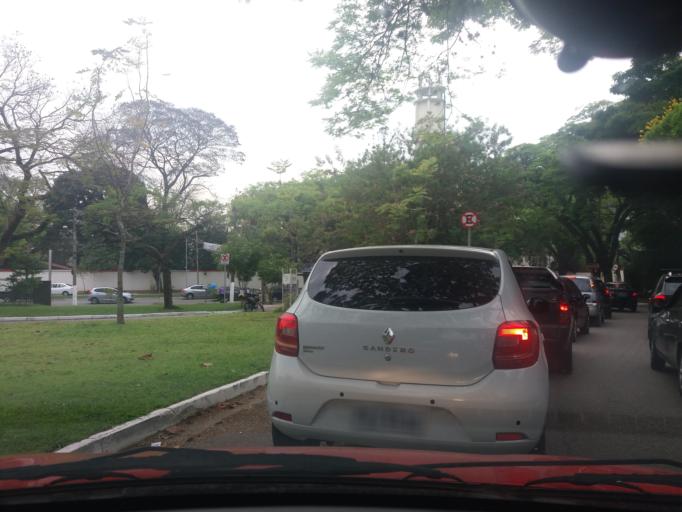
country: BR
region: Sao Paulo
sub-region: Sao Paulo
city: Sao Paulo
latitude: -23.5803
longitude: -46.7018
